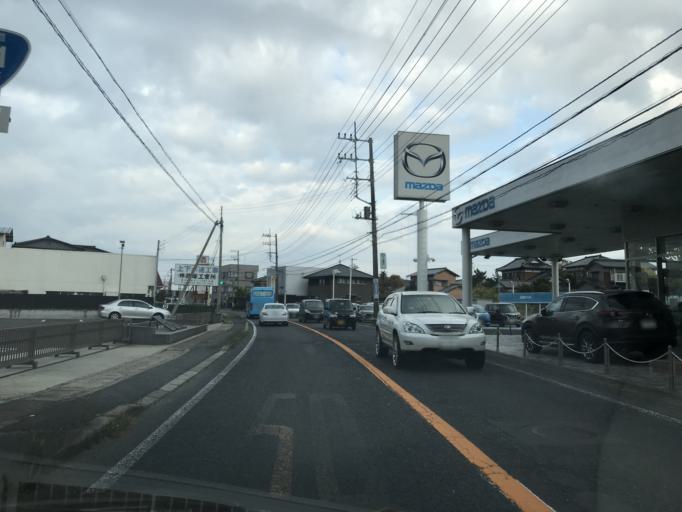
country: JP
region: Ibaraki
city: Itako
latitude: 35.9568
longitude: 140.5864
